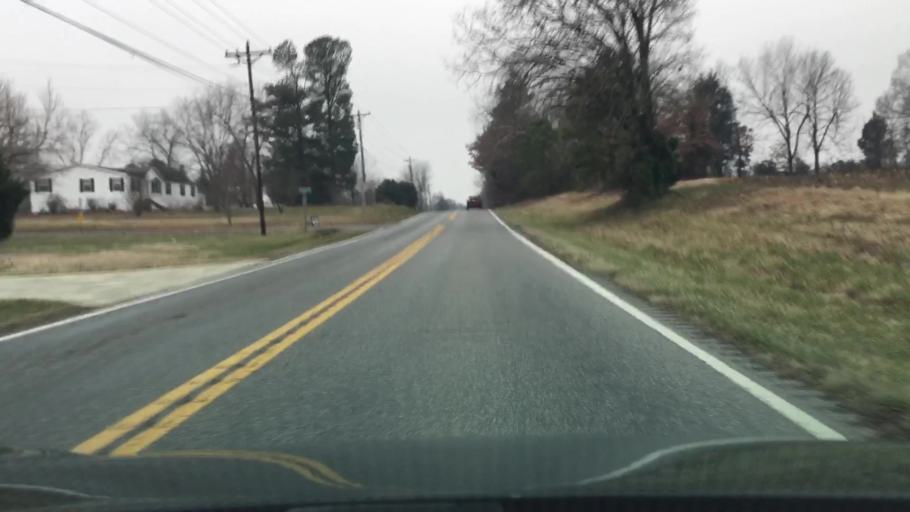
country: US
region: Kentucky
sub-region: Livingston County
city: Ledbetter
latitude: 36.9663
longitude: -88.4412
